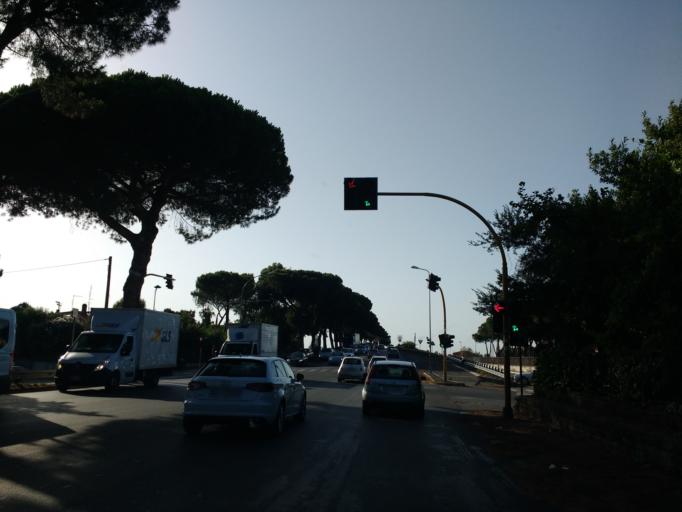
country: IT
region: Latium
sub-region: Citta metropolitana di Roma Capitale
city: Ciampino
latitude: 41.7752
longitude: 12.6086
